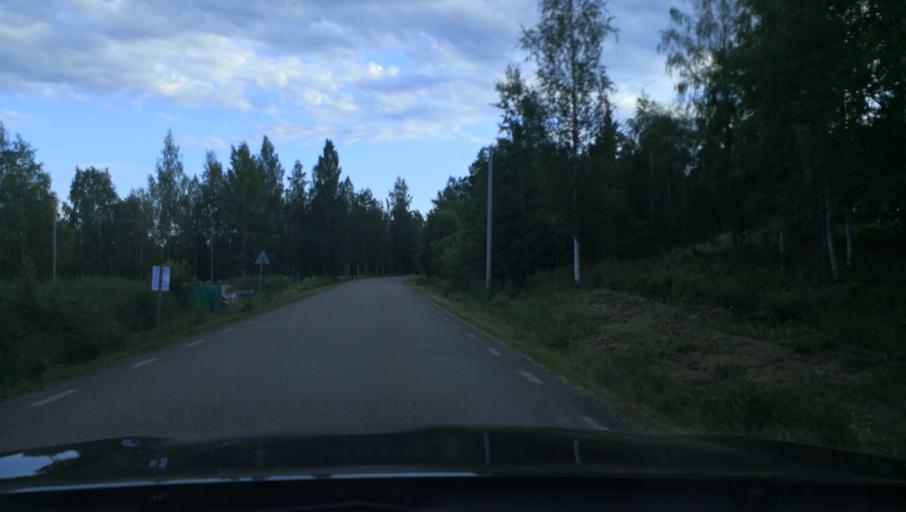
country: SE
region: Dalarna
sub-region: Ludvika Kommun
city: Ludvika
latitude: 60.1151
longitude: 15.2476
